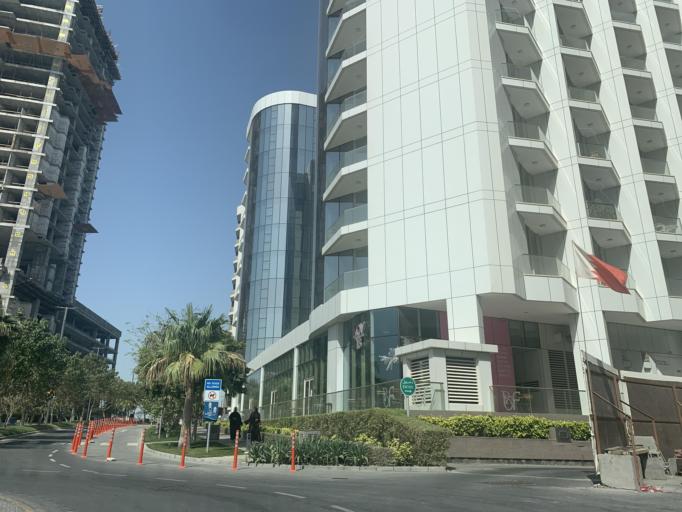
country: BH
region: Manama
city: Manama
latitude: 26.2478
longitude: 50.5777
